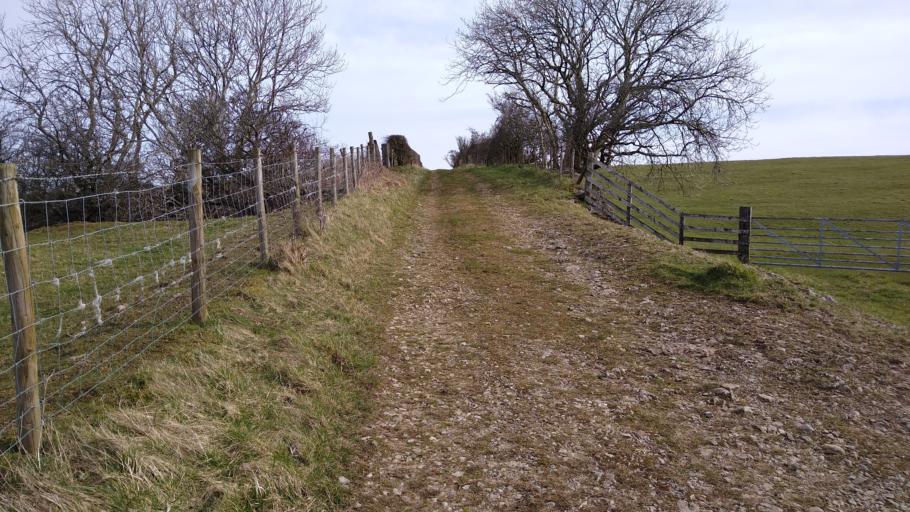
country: GB
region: England
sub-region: Cumbria
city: Cockermouth
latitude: 54.7092
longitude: -3.3674
